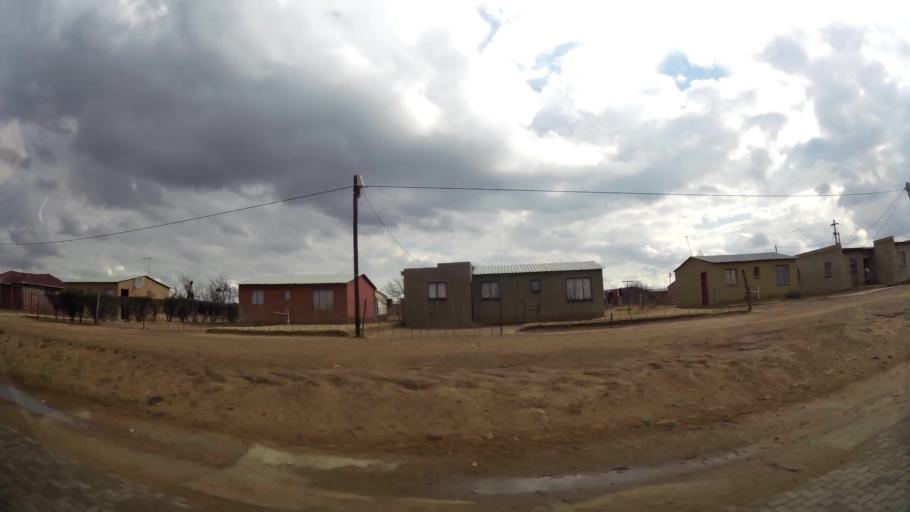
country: ZA
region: Orange Free State
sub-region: Fezile Dabi District Municipality
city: Sasolburg
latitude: -26.8815
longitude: 27.8815
